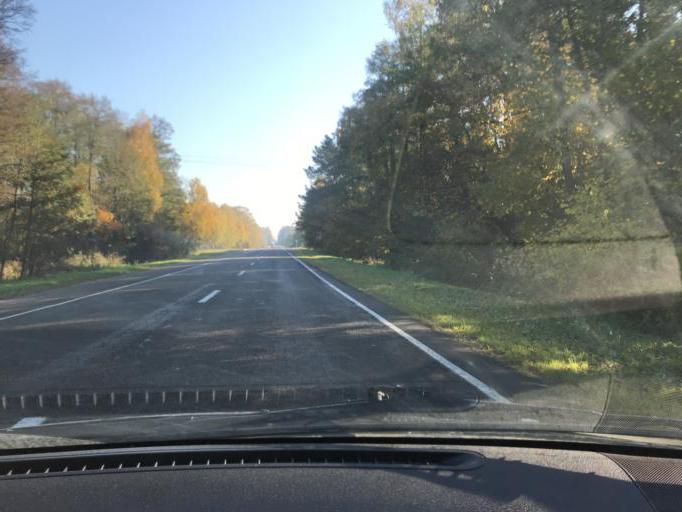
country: BY
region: Brest
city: Lyakhavichy
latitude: 52.9519
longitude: 26.1998
